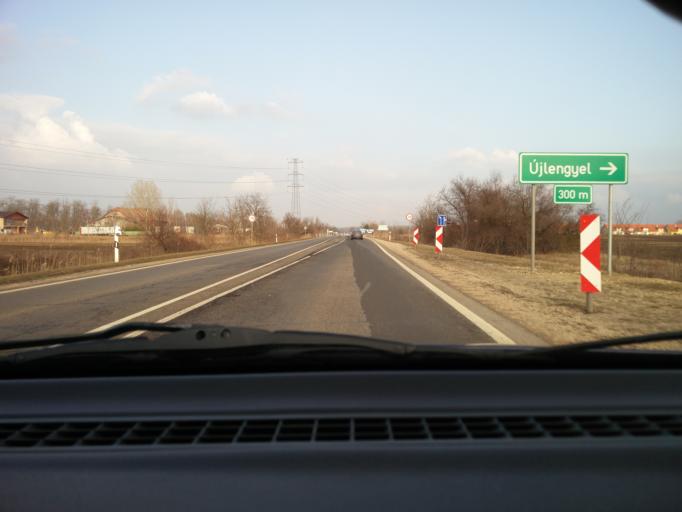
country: HU
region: Pest
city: Ujhartyan
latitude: 47.2402
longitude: 19.4359
